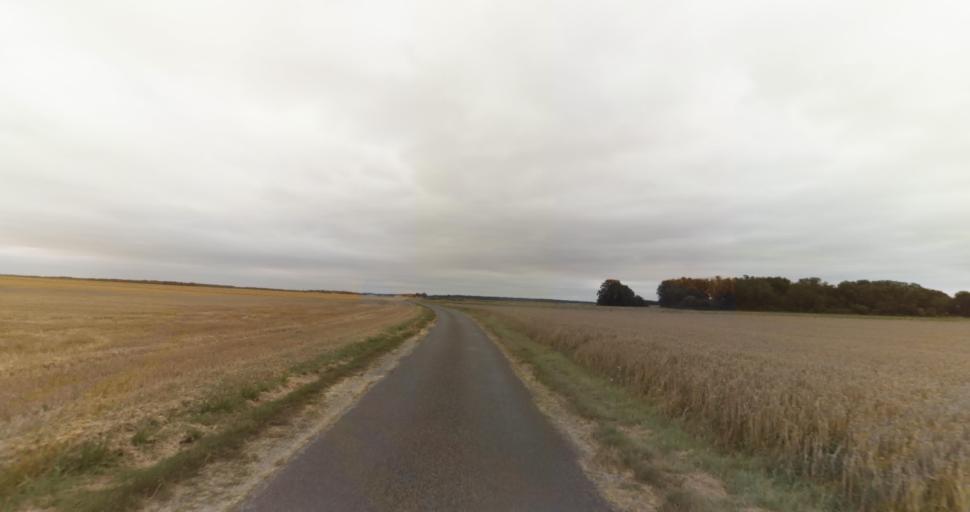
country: FR
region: Haute-Normandie
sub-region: Departement de l'Eure
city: La Couture-Boussey
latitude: 48.9167
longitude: 1.3913
